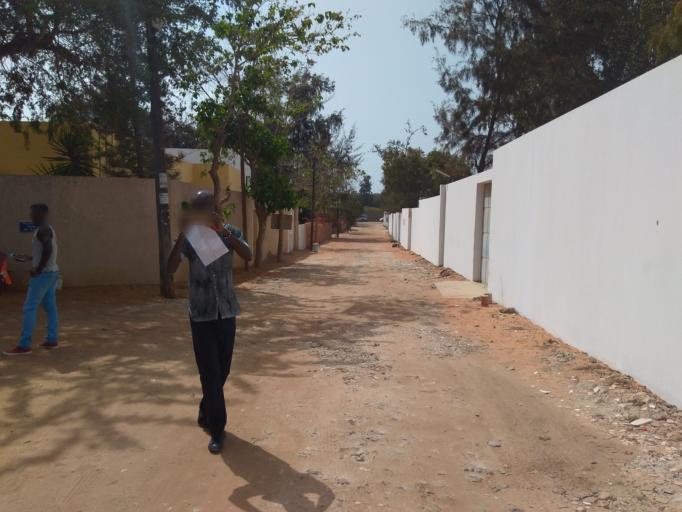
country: SN
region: Dakar
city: Grand Dakar
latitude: 14.7309
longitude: -17.4368
